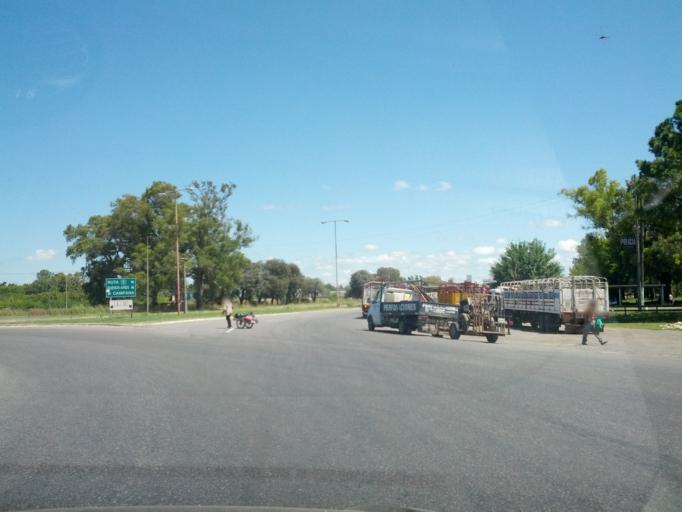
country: AR
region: Buenos Aires
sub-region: Partido de Zarate
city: Zarate
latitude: -34.1216
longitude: -59.0183
